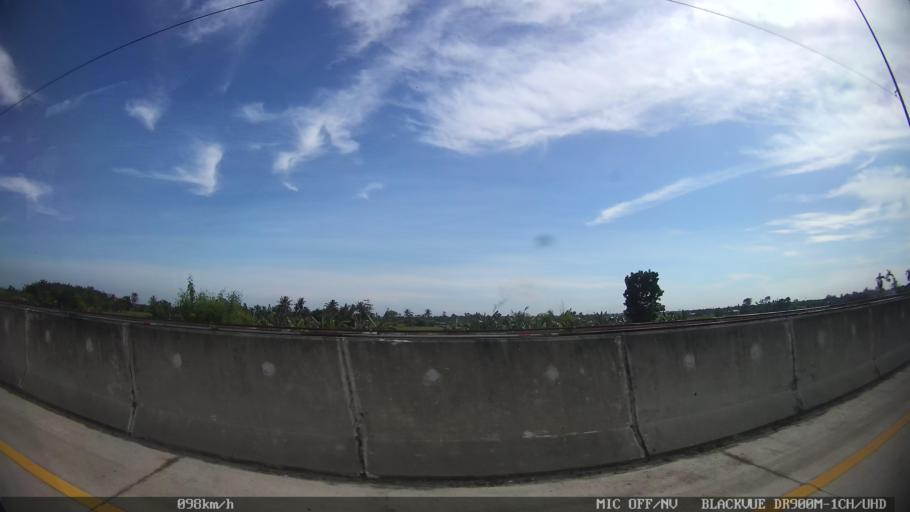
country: ID
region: North Sumatra
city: Sunggal
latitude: 3.6400
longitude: 98.5711
